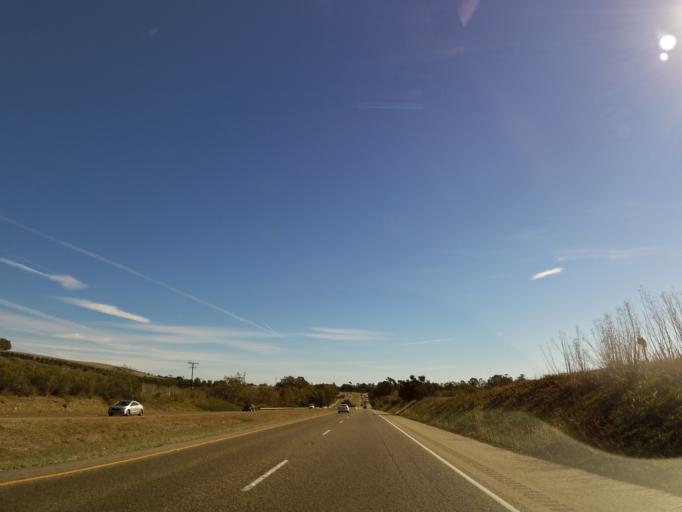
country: US
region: California
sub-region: Santa Barbara County
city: Isla Vista
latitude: 34.4502
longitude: -119.9630
